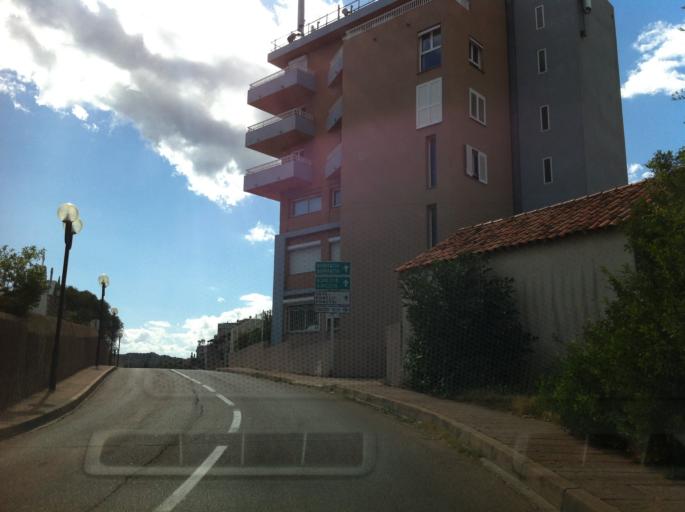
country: FR
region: Corsica
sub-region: Departement de la Corse-du-Sud
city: Porto-Vecchio
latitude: 41.5875
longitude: 9.2770
